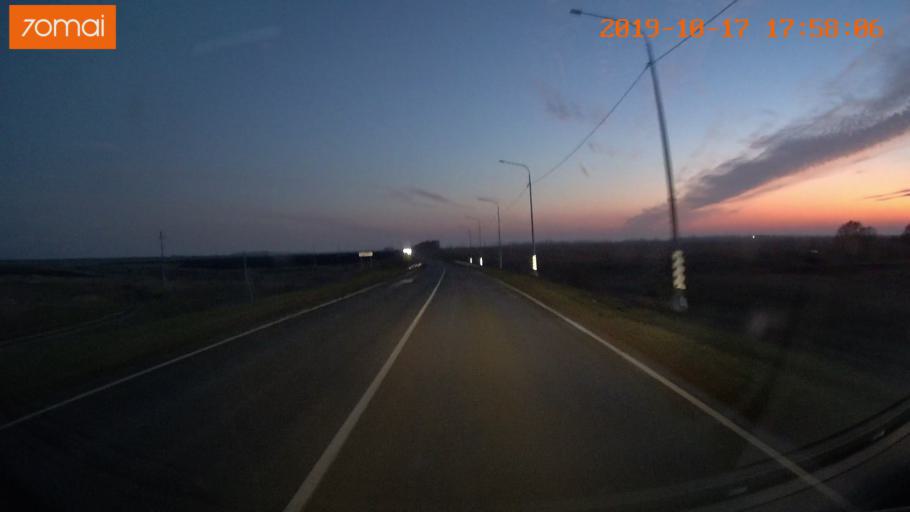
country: RU
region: Tula
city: Kurkino
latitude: 53.5590
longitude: 38.6301
